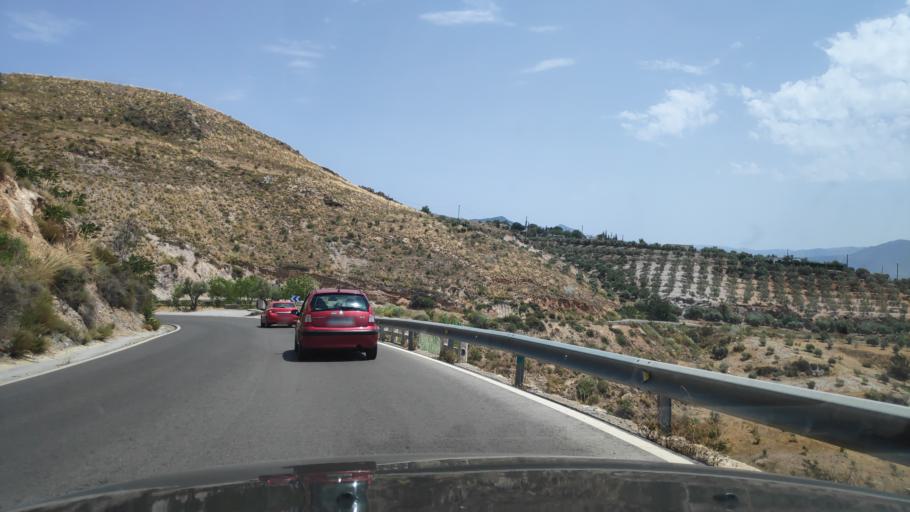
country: ES
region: Andalusia
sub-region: Provincia de Granada
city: Orjiva
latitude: 36.9044
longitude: -3.4467
